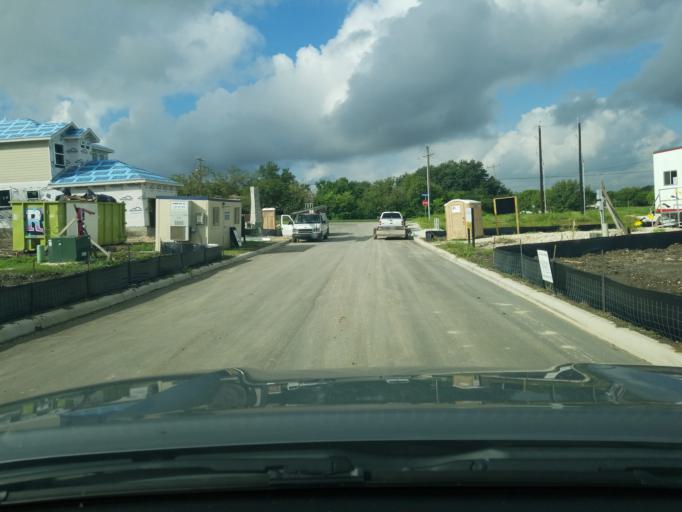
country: US
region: Texas
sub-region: Bexar County
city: Live Oak
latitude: 29.5779
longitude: -98.3609
